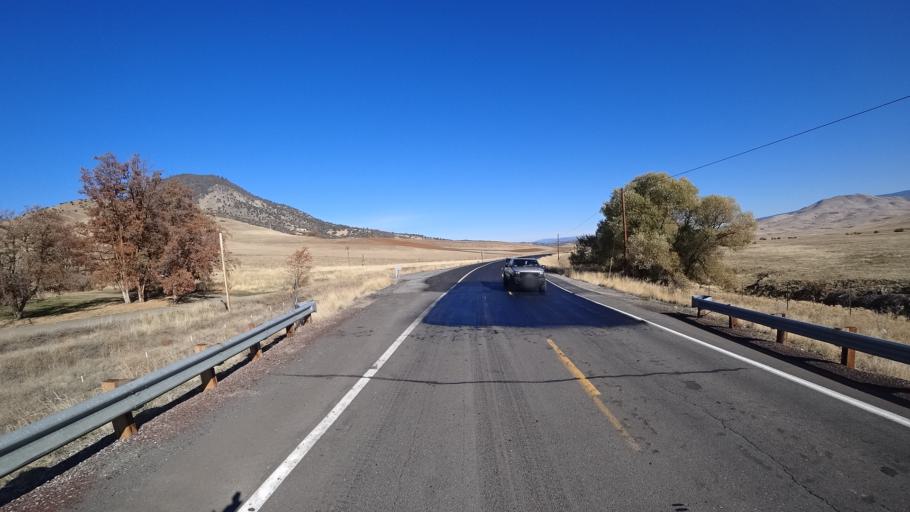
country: US
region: California
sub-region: Siskiyou County
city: Montague
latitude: 41.8279
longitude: -122.4937
